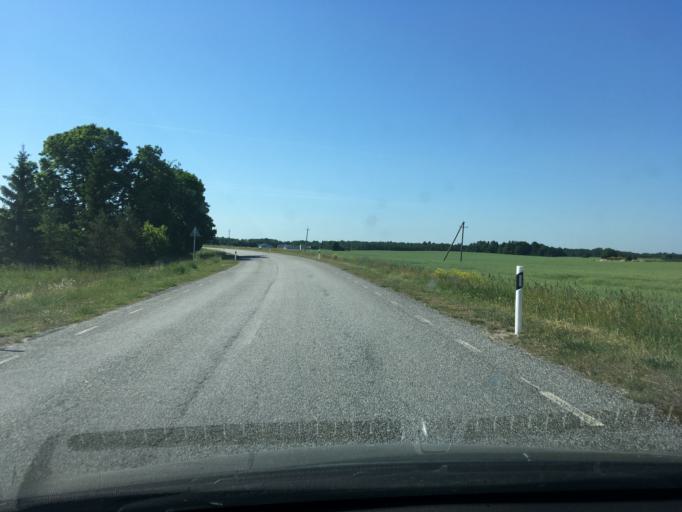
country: EE
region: Harju
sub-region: Raasiku vald
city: Raasiku
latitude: 59.3954
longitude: 25.1867
